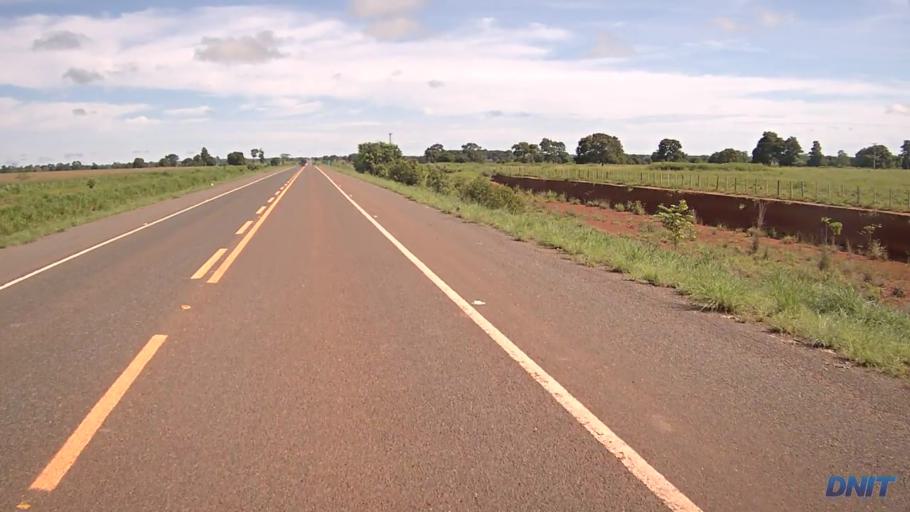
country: BR
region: Goias
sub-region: Sao Miguel Do Araguaia
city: Sao Miguel do Araguaia
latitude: -13.3920
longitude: -50.1376
